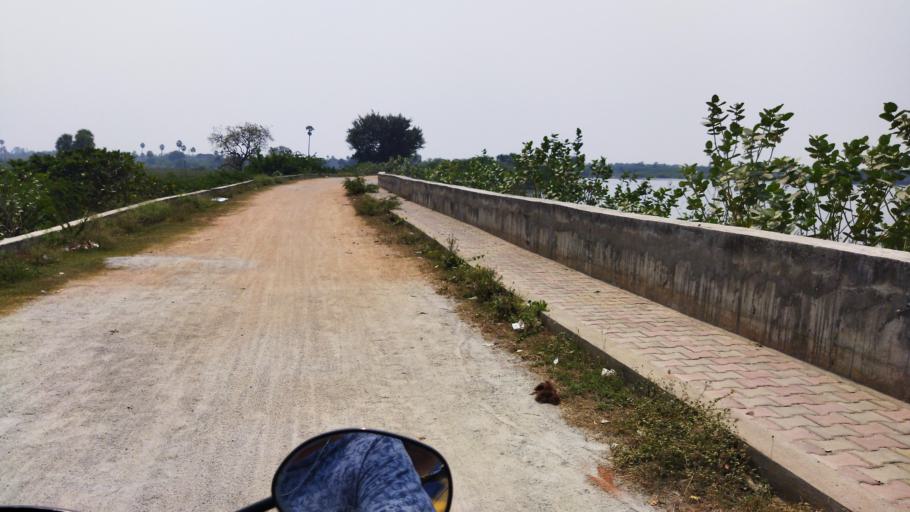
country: IN
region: Telangana
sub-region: Nalgonda
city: Nalgonda
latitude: 17.1651
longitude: 79.4208
